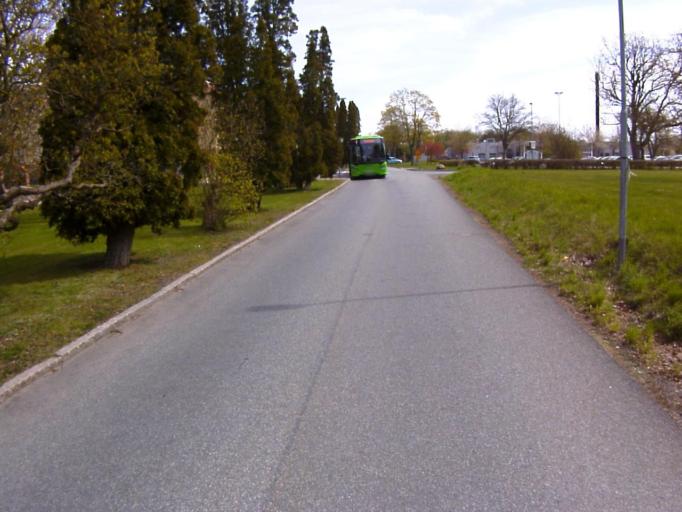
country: SE
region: Skane
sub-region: Kristianstads Kommun
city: Kristianstad
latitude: 56.0469
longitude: 14.1455
